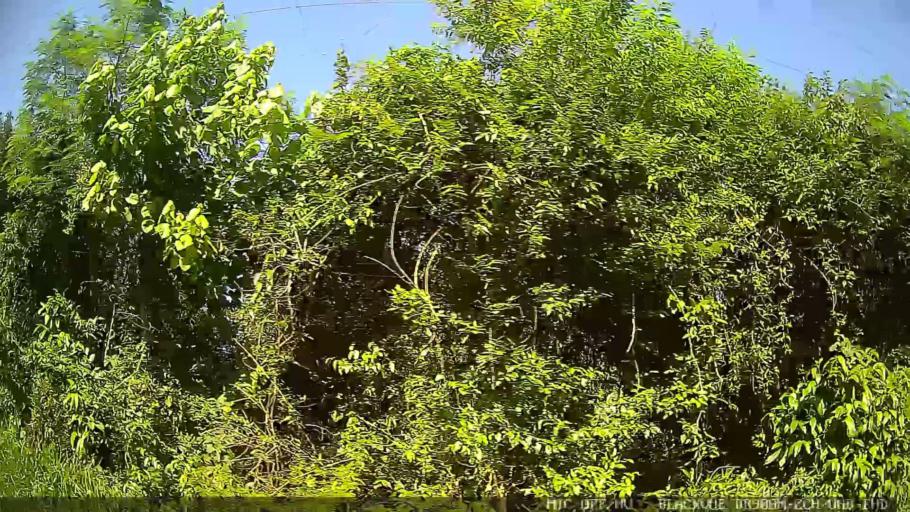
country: BR
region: Sao Paulo
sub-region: Guaruja
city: Guaruja
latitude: -24.0054
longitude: -46.2820
